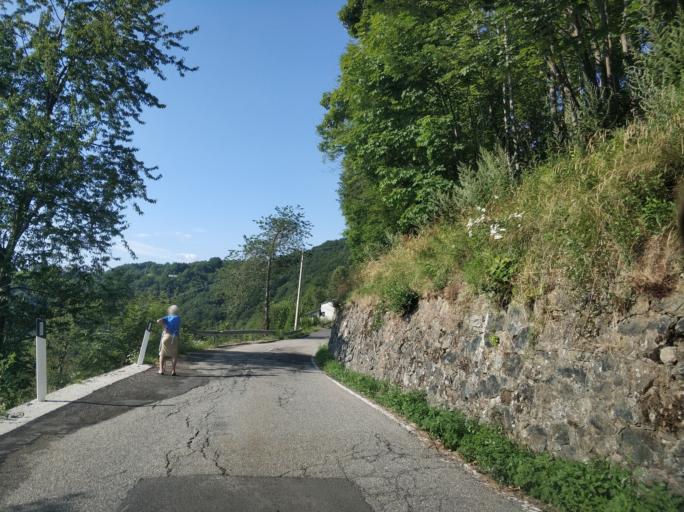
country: IT
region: Piedmont
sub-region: Provincia di Torino
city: Viu
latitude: 45.2150
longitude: 7.3768
